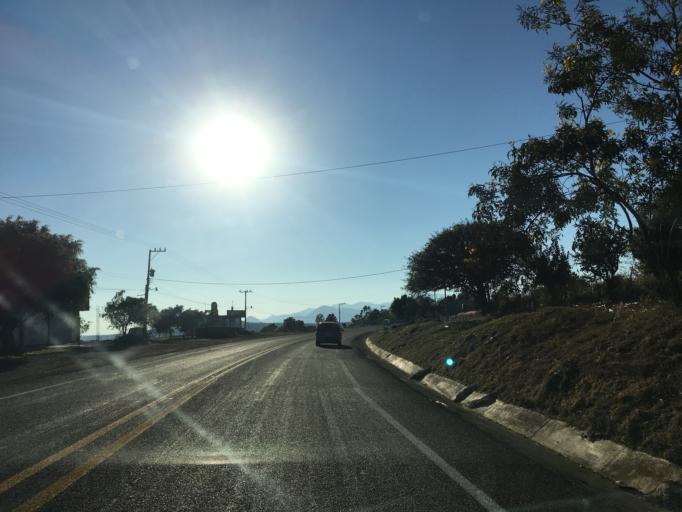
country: MX
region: Michoacan
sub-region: Zitacuaro
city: Puentecillas (Tercera Manzana de Zirahuato)
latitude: 19.4798
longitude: -100.4284
